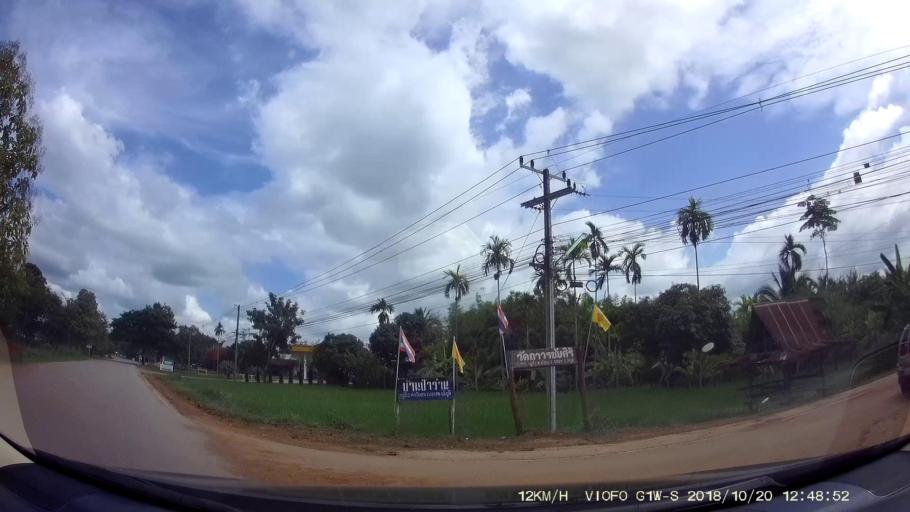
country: TH
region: Chaiyaphum
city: Khon San
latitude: 16.5369
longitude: 101.8941
